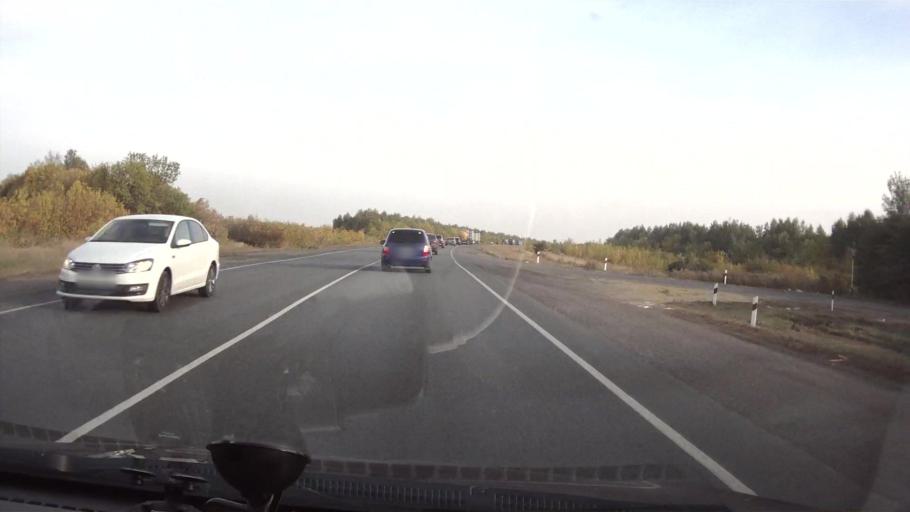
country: RU
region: Saratov
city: Sokolovyy
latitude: 51.5328
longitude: 45.8021
